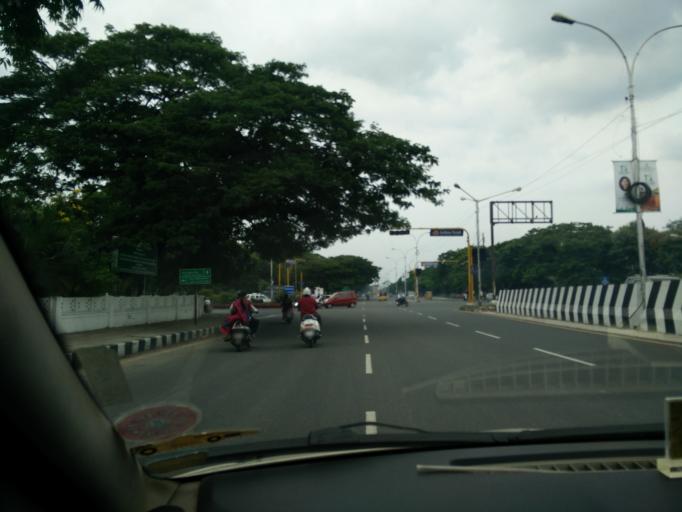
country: IN
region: Tamil Nadu
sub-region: Chennai
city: Chennai
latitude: 13.0734
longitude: 80.2760
